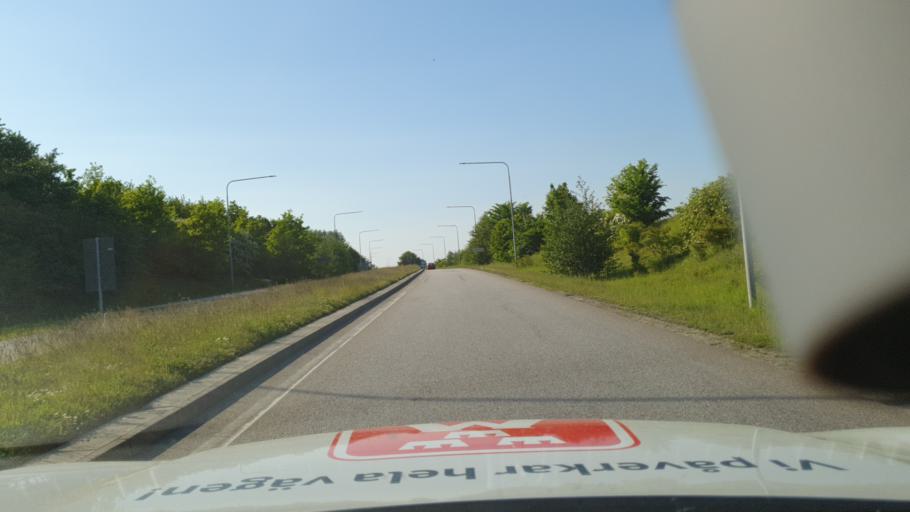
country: SE
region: Skane
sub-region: Burlovs Kommun
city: Arloev
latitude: 55.6370
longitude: 13.0931
